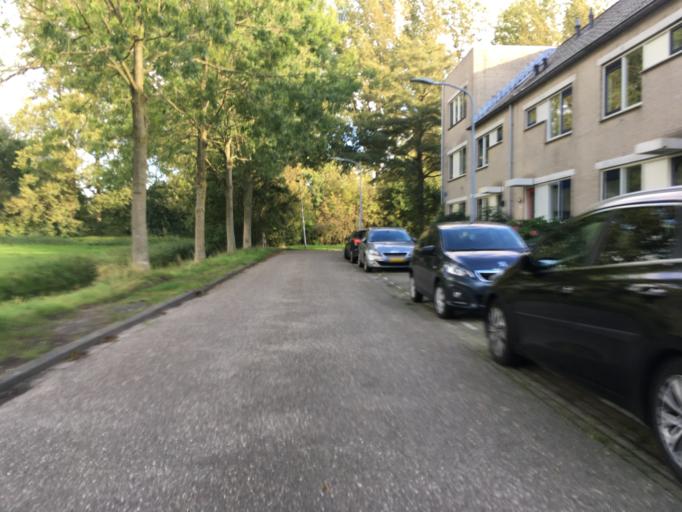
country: NL
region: North Holland
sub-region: Gemeente Haarlem
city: Haarlem
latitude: 52.3766
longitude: 4.6703
